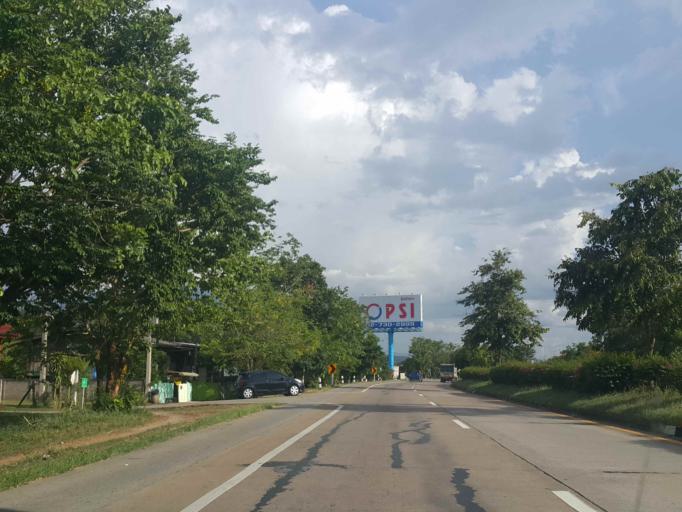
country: TH
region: Phrae
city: Sung Men
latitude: 18.0263
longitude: 100.1111
